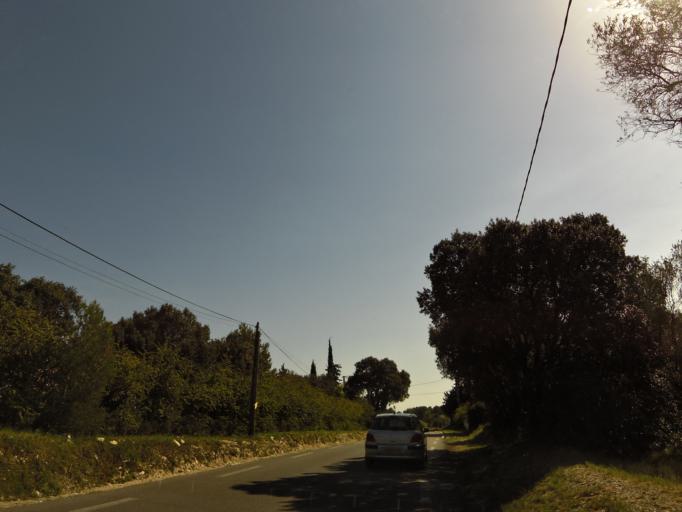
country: FR
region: Languedoc-Roussillon
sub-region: Departement du Gard
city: Aubais
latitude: 43.7424
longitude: 4.1455
